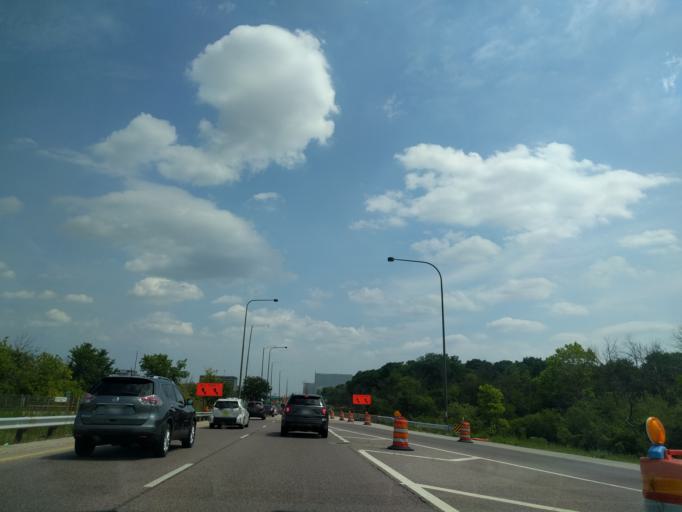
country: US
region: Illinois
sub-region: Cook County
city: Rosemont
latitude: 41.9835
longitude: -87.8576
